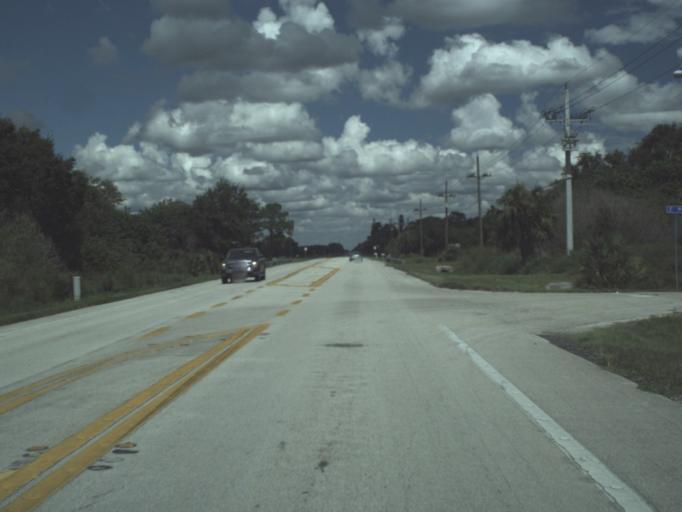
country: US
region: Florida
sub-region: Hendry County
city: LaBelle
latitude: 26.6715
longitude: -81.4364
